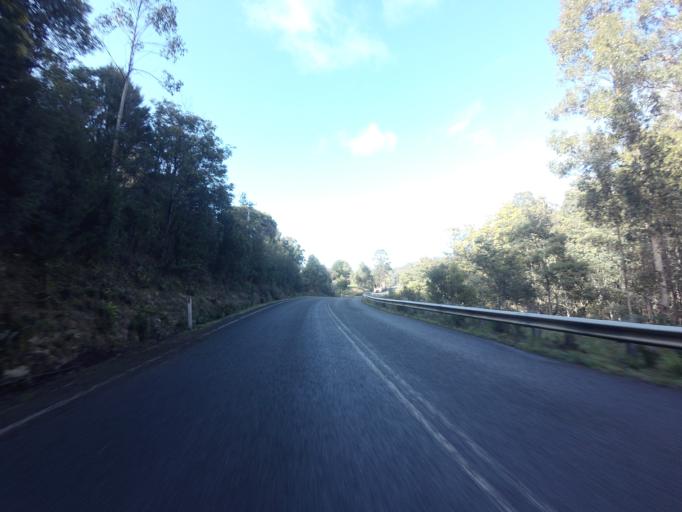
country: AU
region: Tasmania
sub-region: Huon Valley
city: Cygnet
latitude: -43.2765
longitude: 147.0089
